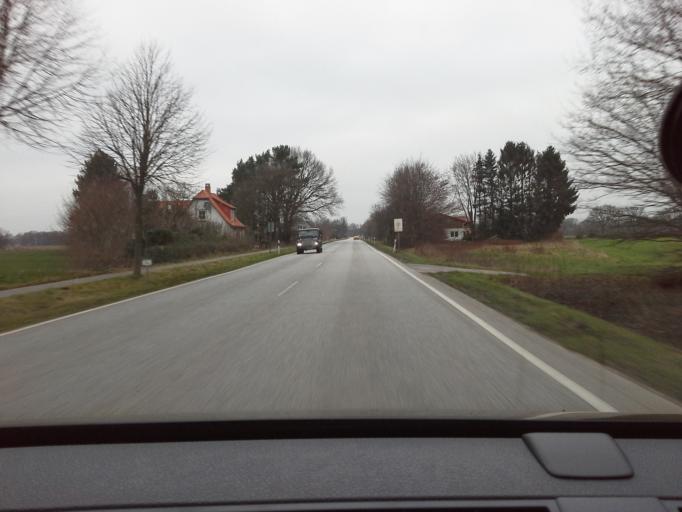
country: DE
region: Schleswig-Holstein
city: Bilsen
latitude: 53.7779
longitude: 9.8754
